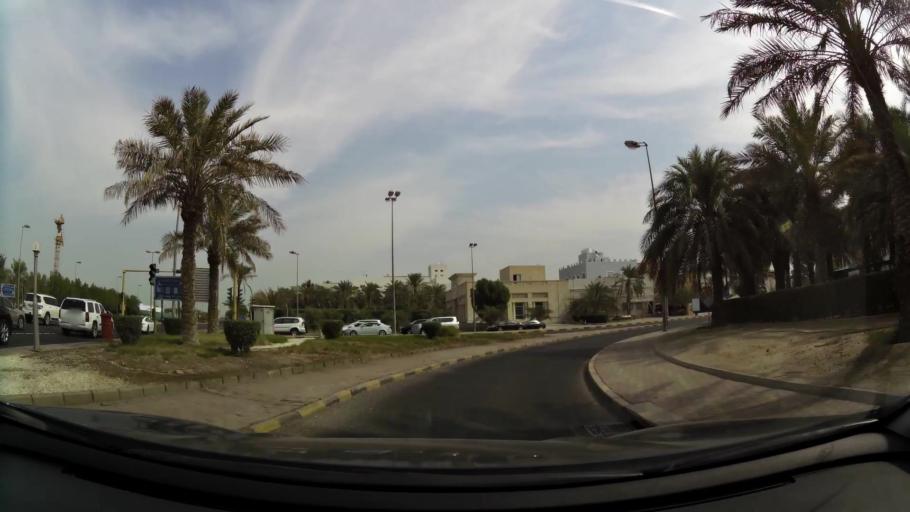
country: KW
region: Al Asimah
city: Ash Shamiyah
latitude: 29.3445
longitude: 47.9792
